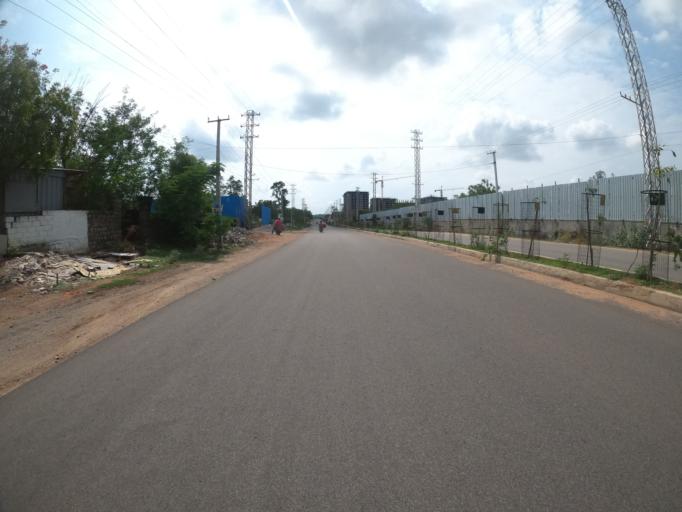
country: IN
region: Telangana
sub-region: Medak
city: Serilingampalle
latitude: 17.3900
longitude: 78.3260
